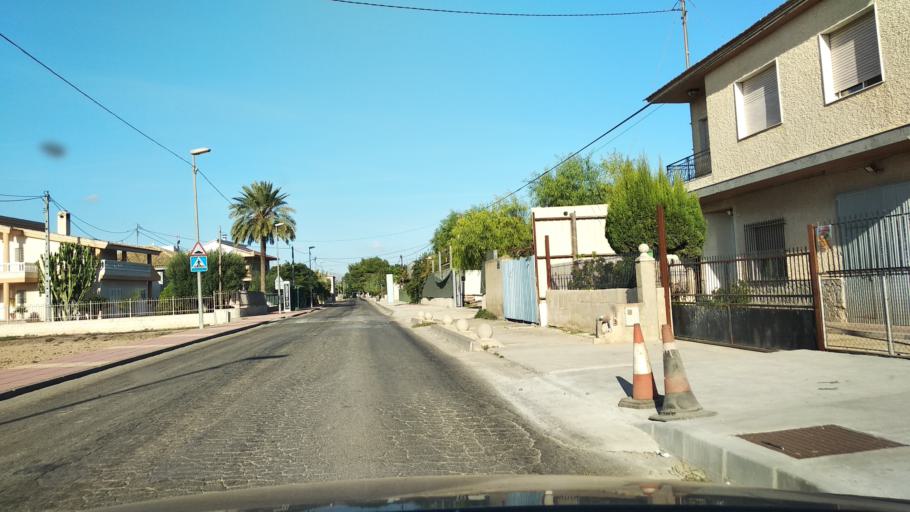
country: ES
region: Murcia
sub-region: Murcia
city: Santomera
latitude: 38.0434
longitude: -1.0411
